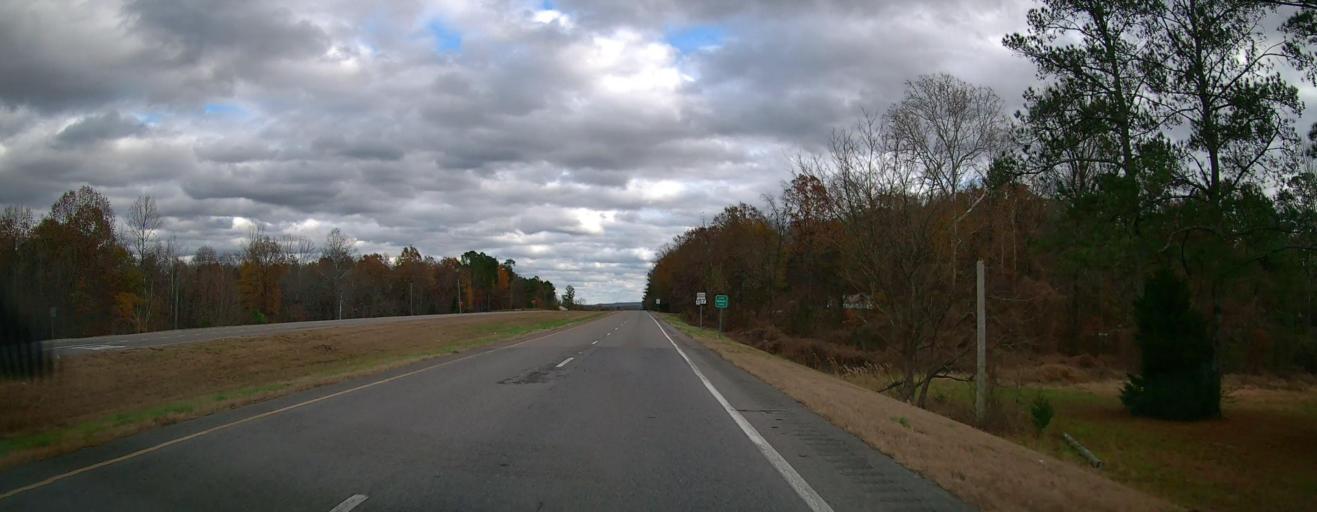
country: US
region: Alabama
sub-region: Morgan County
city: Danville
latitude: 34.3888
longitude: -87.1104
